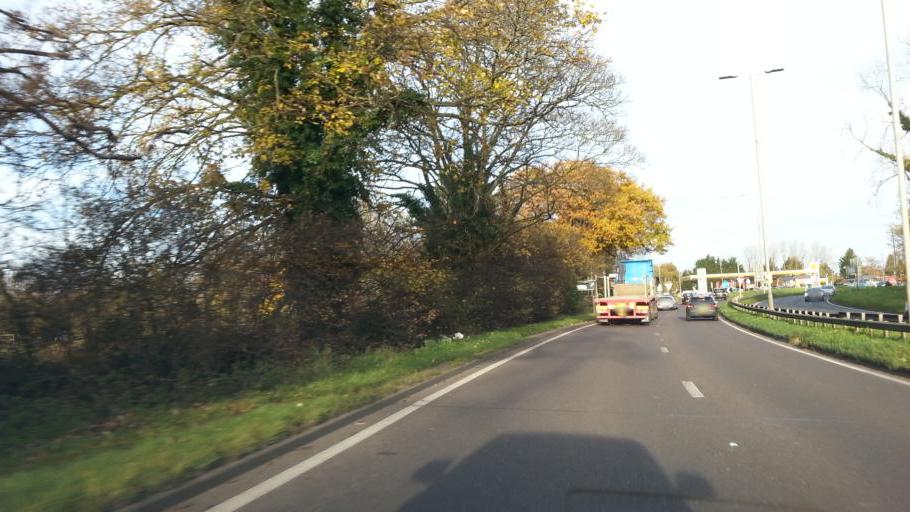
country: GB
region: England
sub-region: Hertfordshire
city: St Albans
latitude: 51.7198
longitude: -0.3664
